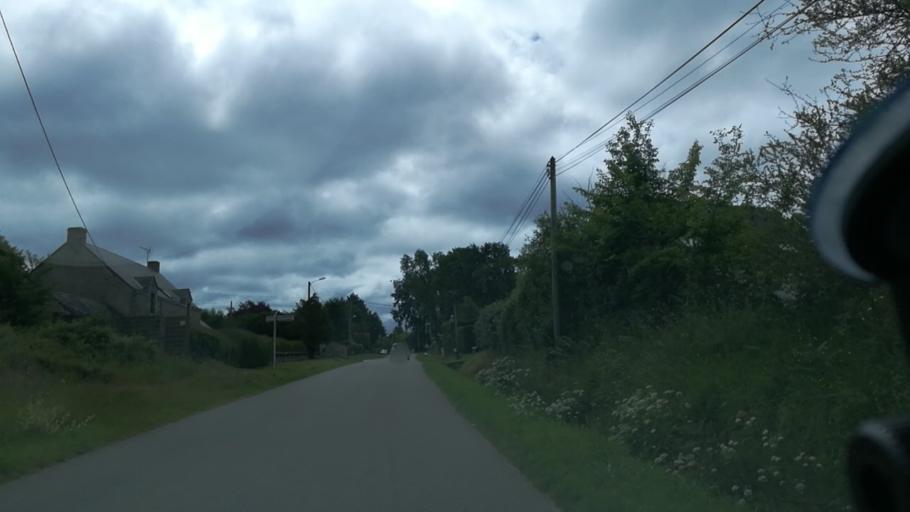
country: FR
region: Brittany
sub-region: Departement du Morbihan
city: Penestin
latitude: 47.4915
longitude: -2.4387
